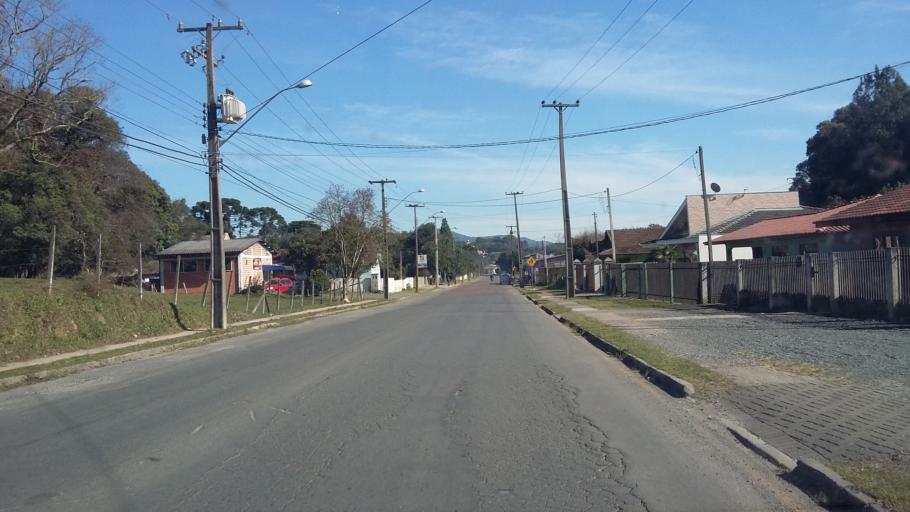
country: BR
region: Parana
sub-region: Campo Largo
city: Campo Largo
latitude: -25.4683
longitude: -49.5671
